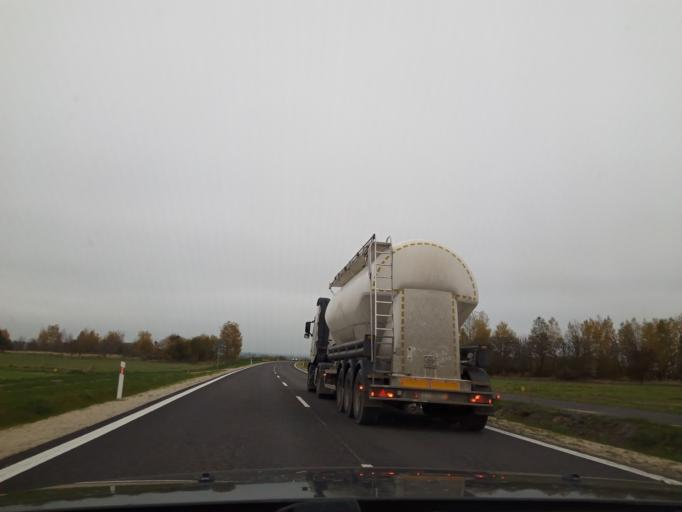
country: PL
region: Swietokrzyskie
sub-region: Powiat jedrzejowski
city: Jedrzejow
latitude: 50.6203
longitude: 20.3147
